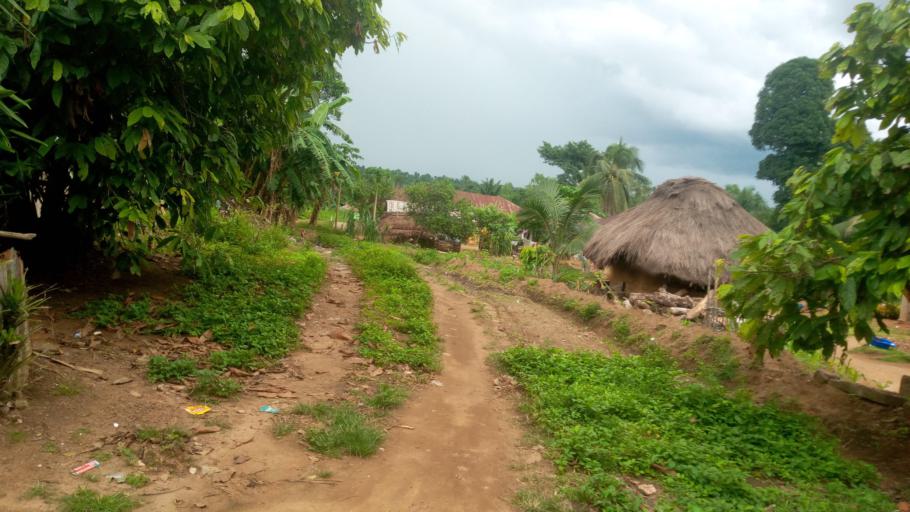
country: SL
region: Southern Province
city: Mogbwemo
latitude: 7.6060
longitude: -12.1696
